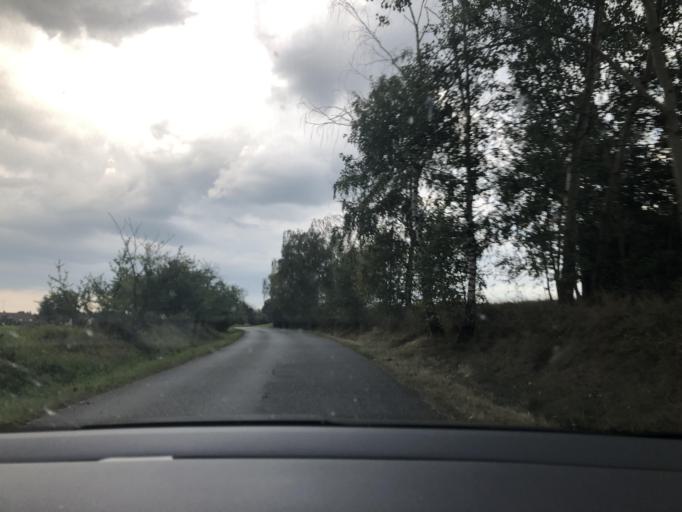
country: CZ
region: Central Bohemia
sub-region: Okres Kolin
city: Tynec nad Labem
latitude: 50.0318
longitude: 15.3573
